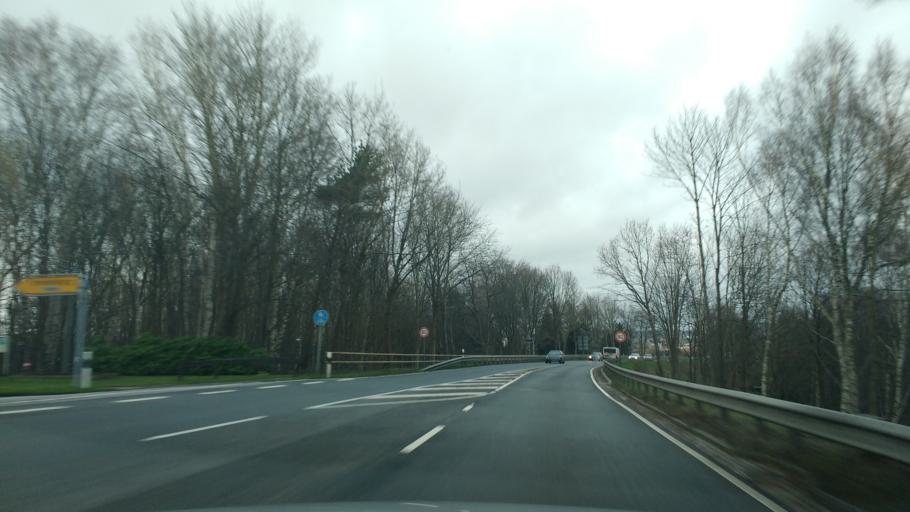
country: DE
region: Schleswig-Holstein
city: Itzehoe
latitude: 53.9060
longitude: 9.5085
